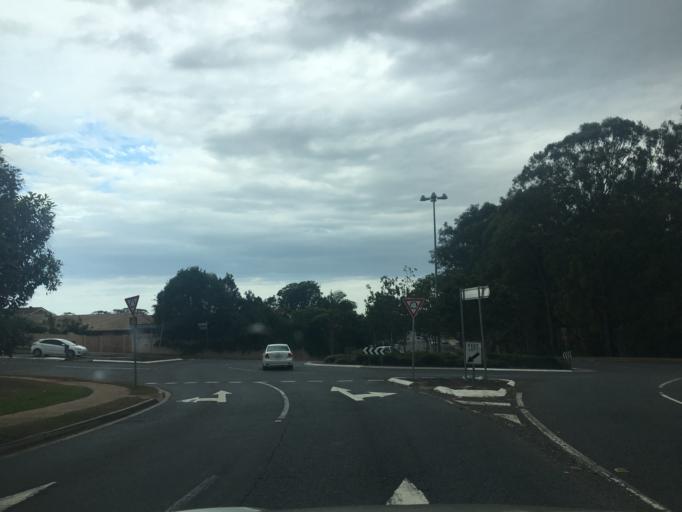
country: AU
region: Queensland
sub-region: Brisbane
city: Taigum
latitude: -27.3474
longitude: 153.0216
